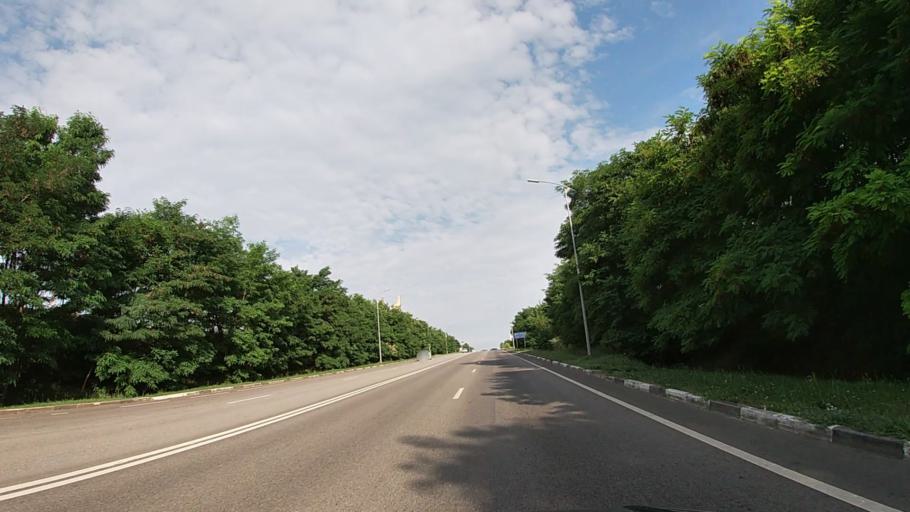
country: RU
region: Belgorod
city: Severnyy
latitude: 50.6365
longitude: 36.4500
